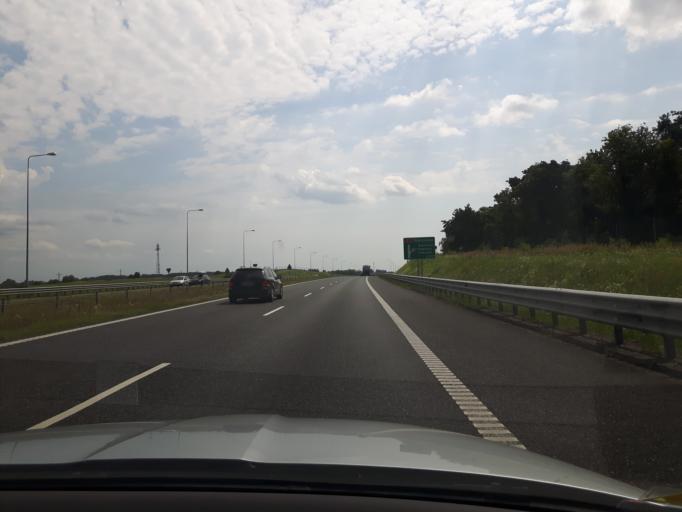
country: PL
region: Warmian-Masurian Voivodeship
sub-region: Powiat olsztynski
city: Olsztynek
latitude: 53.5066
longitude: 20.3076
